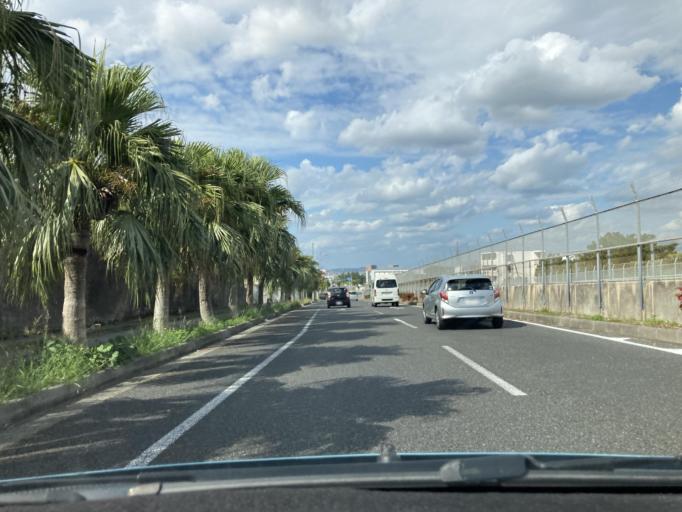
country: JP
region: Okinawa
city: Okinawa
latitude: 26.3270
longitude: 127.7861
